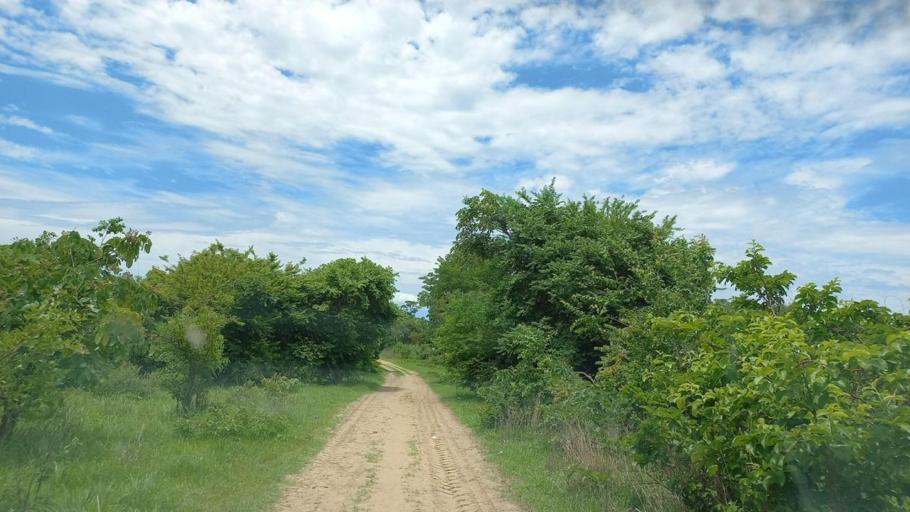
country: ZM
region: North-Western
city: Kabompo
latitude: -13.6222
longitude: 24.1917
